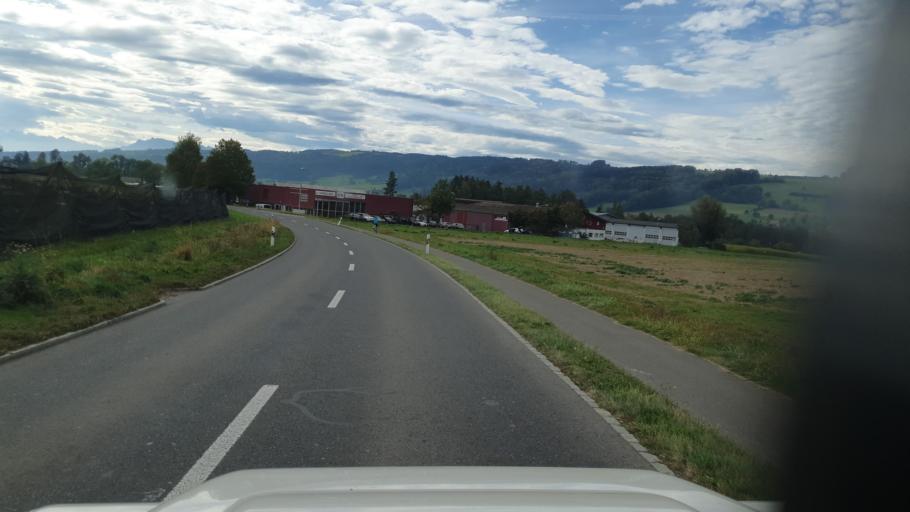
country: CH
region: Lucerne
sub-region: Hochdorf District
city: Hitzkirch
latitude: 47.2506
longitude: 8.2375
